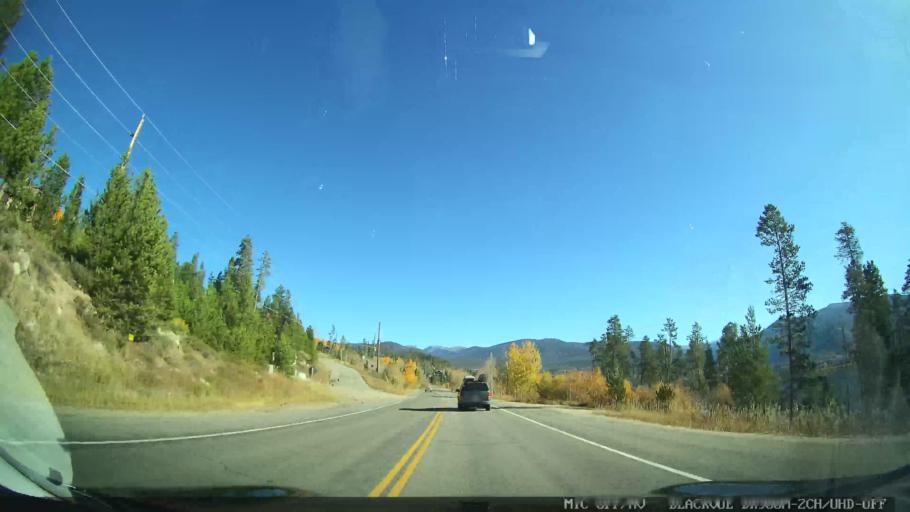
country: US
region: Colorado
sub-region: Grand County
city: Granby
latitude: 40.2414
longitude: -105.8446
